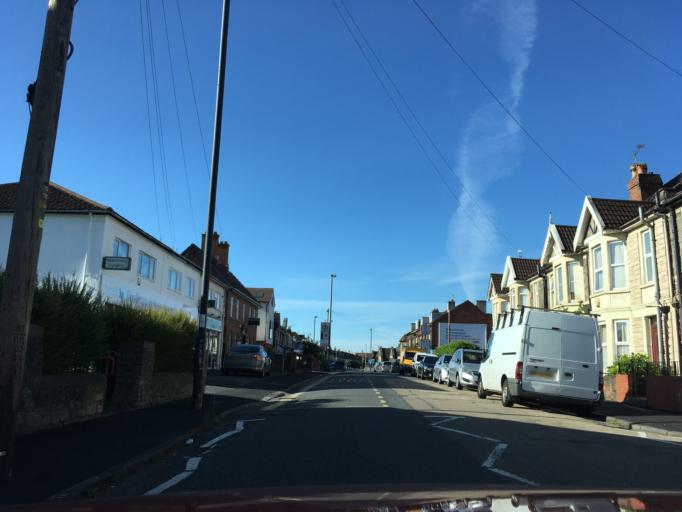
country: GB
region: England
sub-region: Bath and North East Somerset
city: Whitchurch
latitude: 51.4394
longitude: -2.5518
